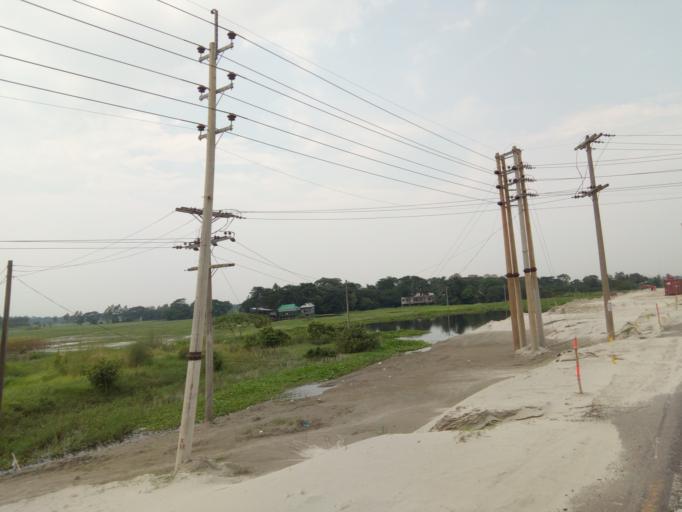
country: BD
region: Dhaka
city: Dohar
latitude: 23.5146
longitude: 90.2782
